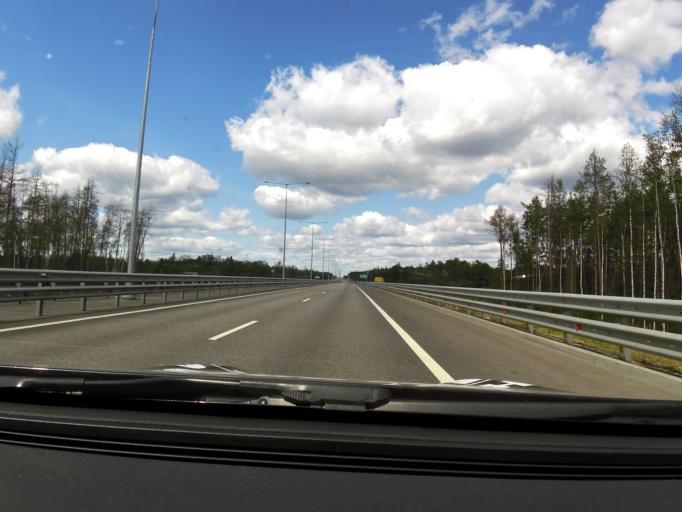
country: RU
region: Tverskaya
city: Krasnomayskiy
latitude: 57.4446
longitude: 34.4324
